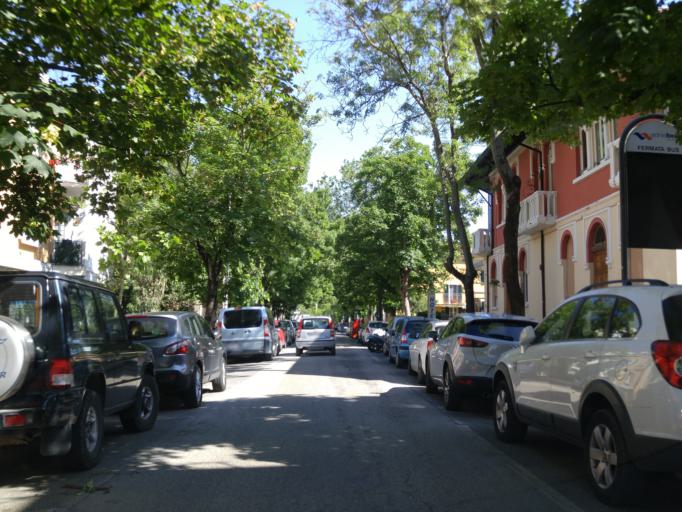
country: IT
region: The Marches
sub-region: Provincia di Pesaro e Urbino
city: Pesaro
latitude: 43.9149
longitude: 12.9148
